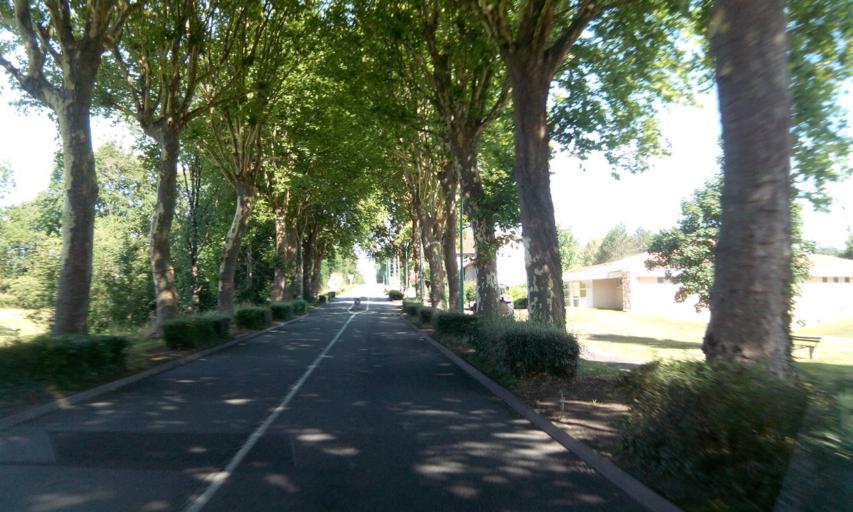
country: FR
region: Poitou-Charentes
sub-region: Departement de la Charente
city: Etagnac
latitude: 45.9338
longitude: 0.7382
